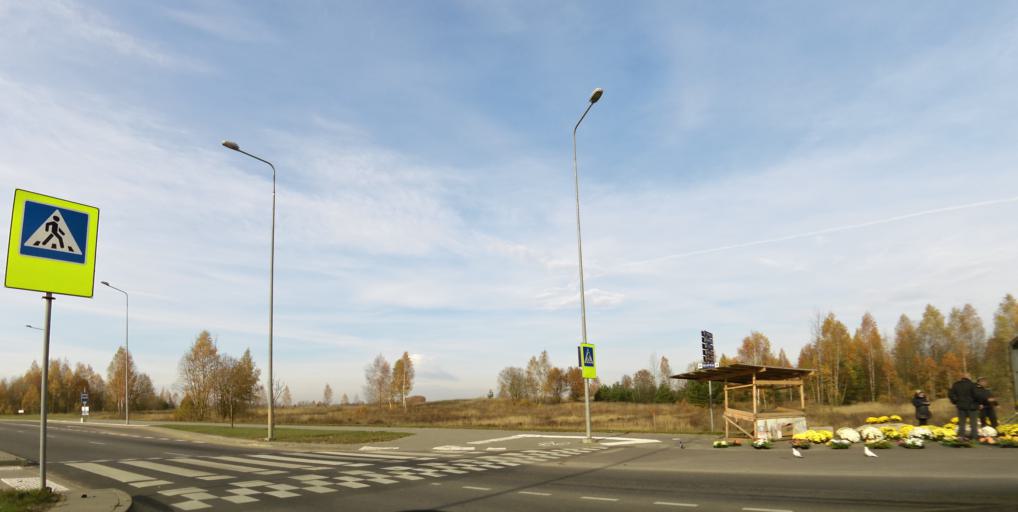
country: LT
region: Vilnius County
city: Pilaite
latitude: 54.7104
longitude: 25.1750
